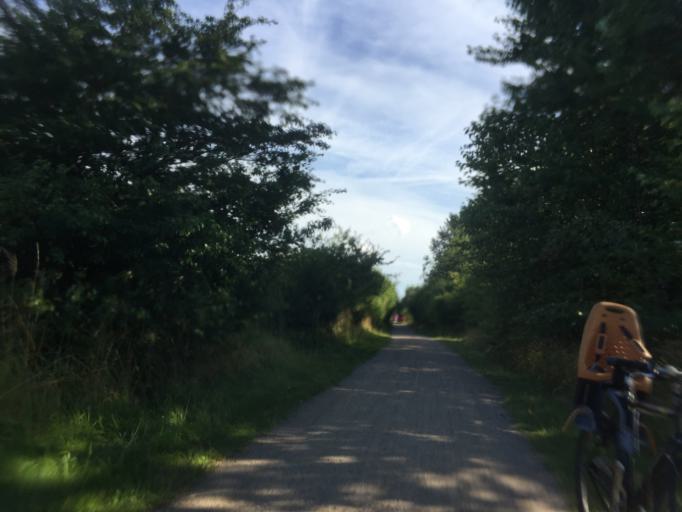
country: DK
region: Capital Region
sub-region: Kobenhavn
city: Christianshavn
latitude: 55.6523
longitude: 12.5832
